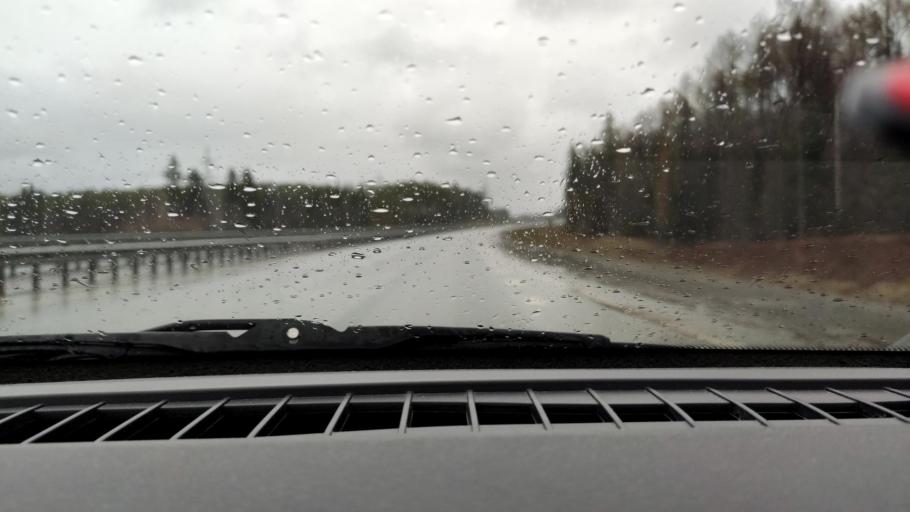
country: RU
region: Perm
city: Ferma
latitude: 58.0122
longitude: 56.4025
